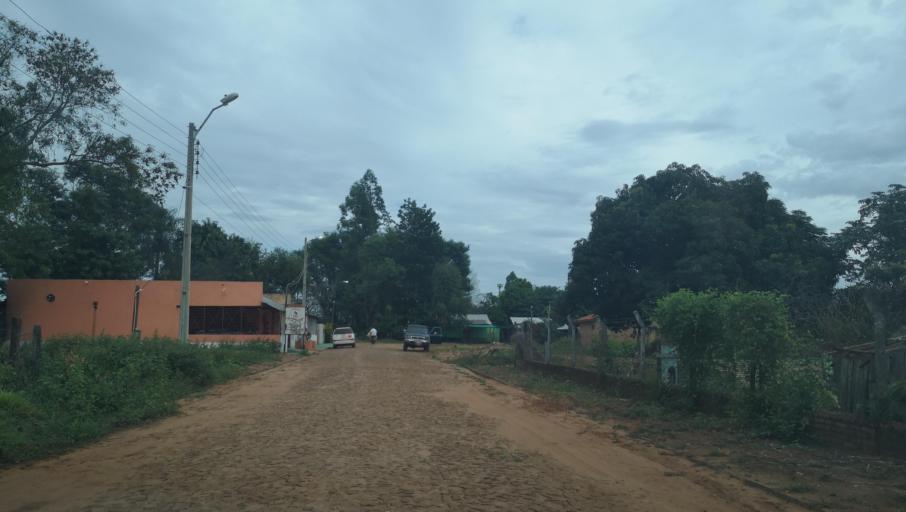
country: PY
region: San Pedro
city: Capiibary
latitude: -24.7376
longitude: -56.0238
